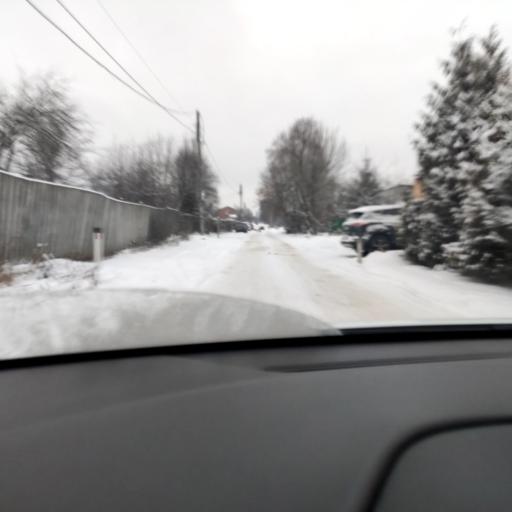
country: RU
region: Tatarstan
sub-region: Gorod Kazan'
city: Kazan
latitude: 55.8380
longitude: 49.2124
